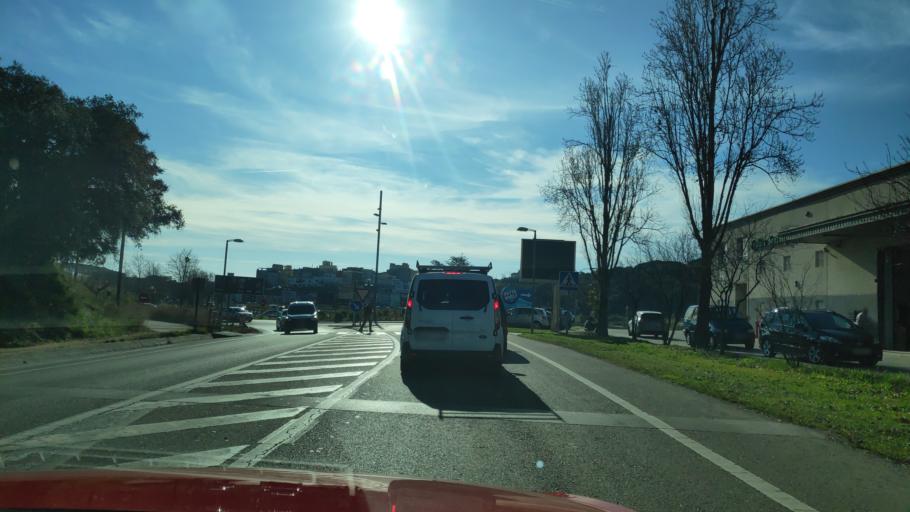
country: ES
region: Catalonia
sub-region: Provincia de Girona
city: Lloret de Mar
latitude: 41.7097
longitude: 2.8322
